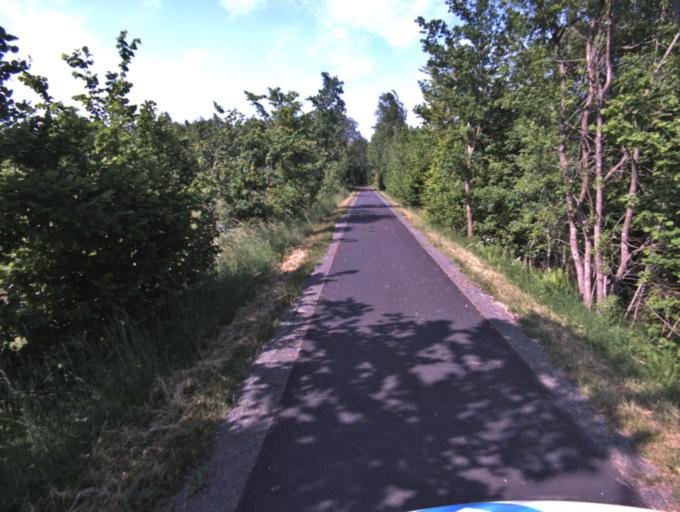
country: SE
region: Skane
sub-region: Kristianstads Kommun
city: Tollarp
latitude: 56.1954
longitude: 14.2892
